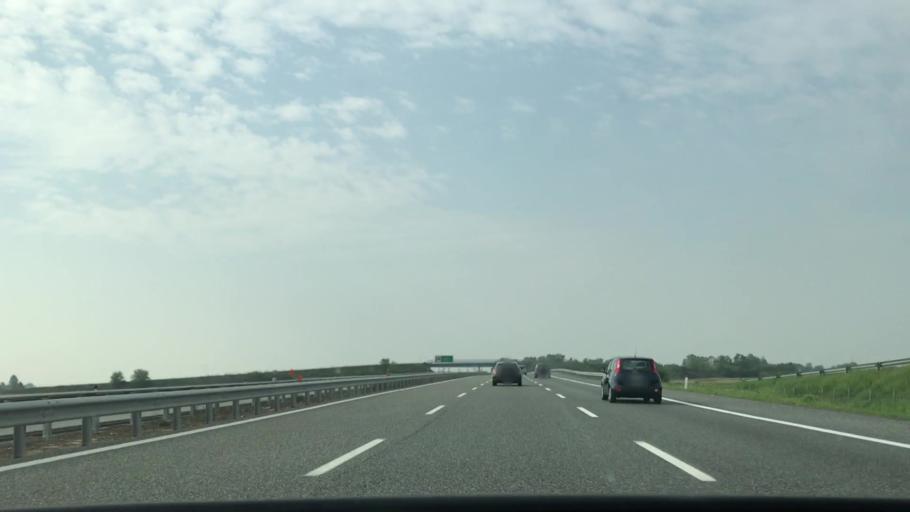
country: IT
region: Piedmont
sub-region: Provincia di Vercelli
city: Prarolo
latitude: 45.2694
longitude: 8.4691
